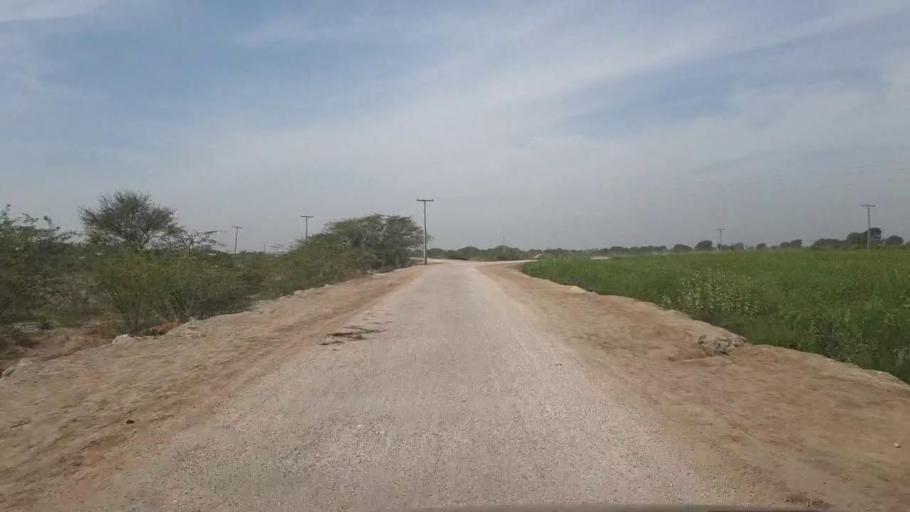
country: PK
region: Sindh
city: Kunri
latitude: 25.2290
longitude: 69.6730
